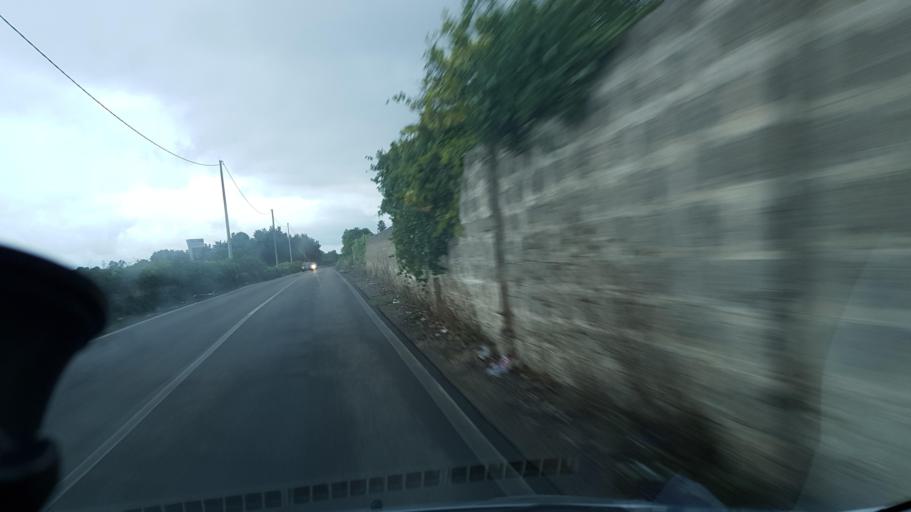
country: IT
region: Apulia
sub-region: Provincia di Lecce
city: Novoli
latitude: 40.3649
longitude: 18.0680
